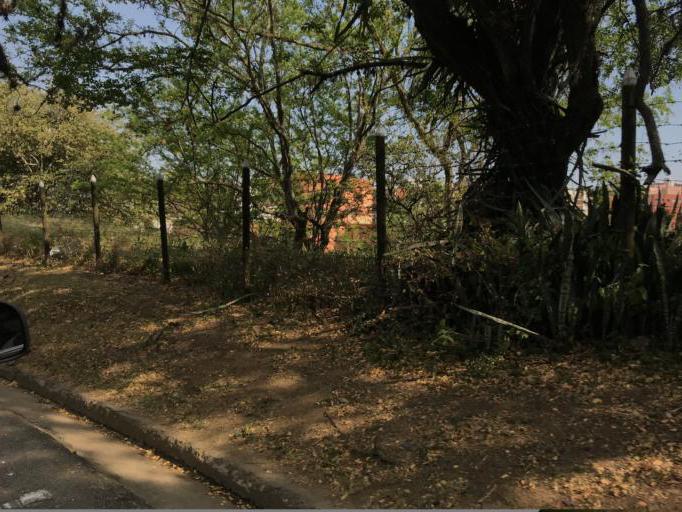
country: CO
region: Valle del Cauca
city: Cali
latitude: 3.4500
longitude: -76.5574
